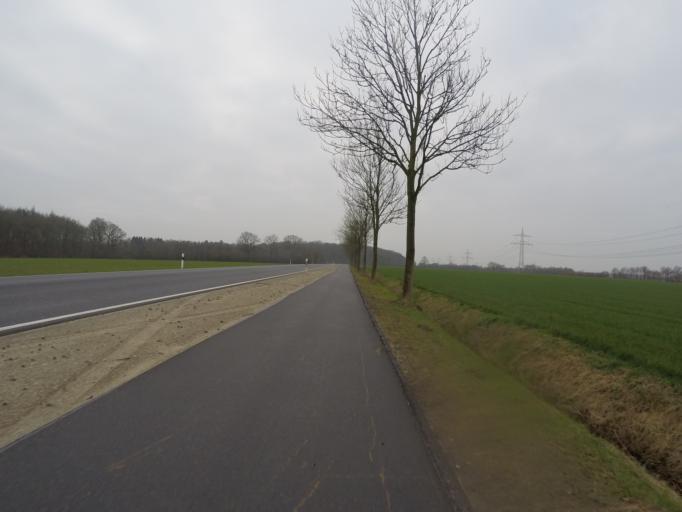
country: DE
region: Schleswig-Holstein
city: Borstel-Hohenraden
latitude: 53.7115
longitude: 9.8460
